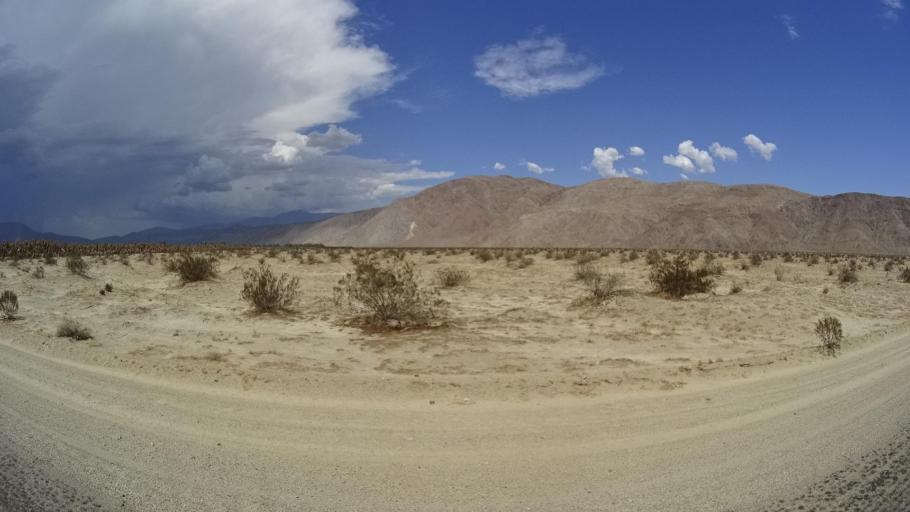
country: US
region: California
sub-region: San Diego County
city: Borrego Springs
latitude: 33.3008
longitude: -116.3385
